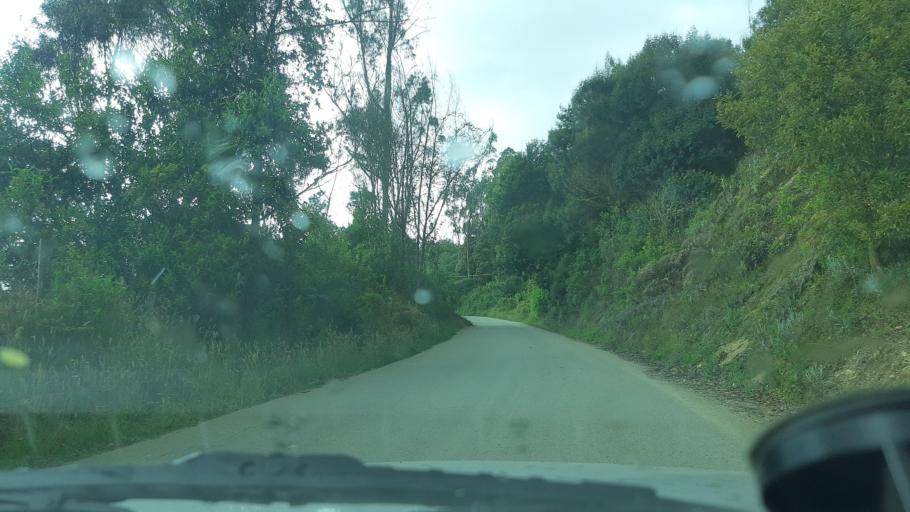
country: CO
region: Cundinamarca
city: Umbita
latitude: 5.2181
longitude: -73.4725
